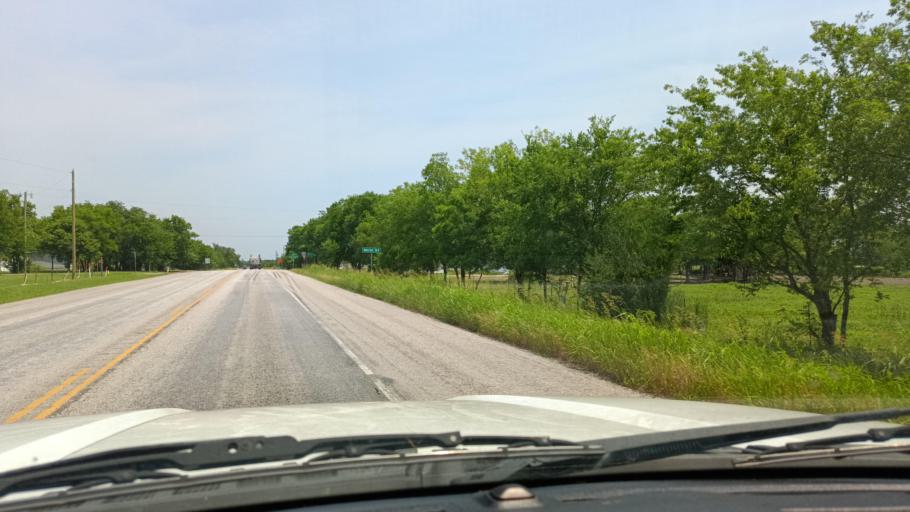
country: US
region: Texas
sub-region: Bell County
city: Rogers
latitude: 30.9445
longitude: -97.2443
